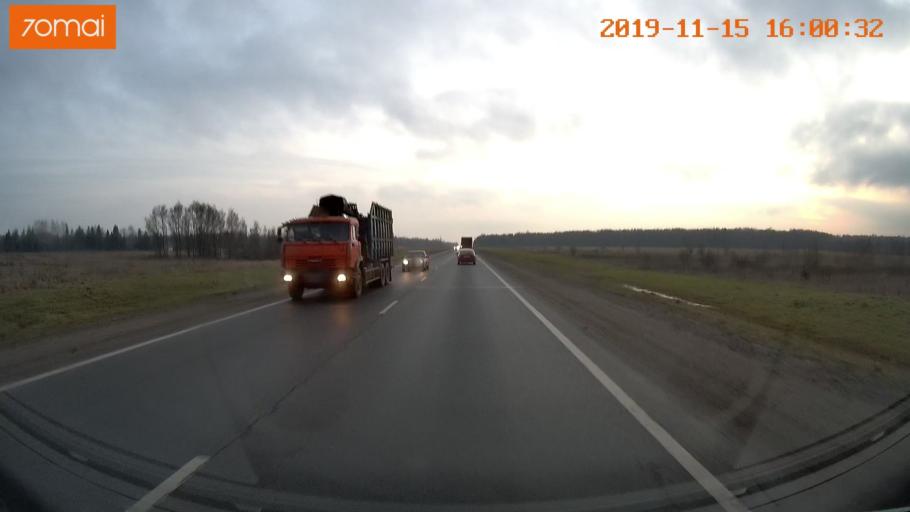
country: RU
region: Jaroslavl
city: Yaroslavl
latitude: 57.7947
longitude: 39.9381
